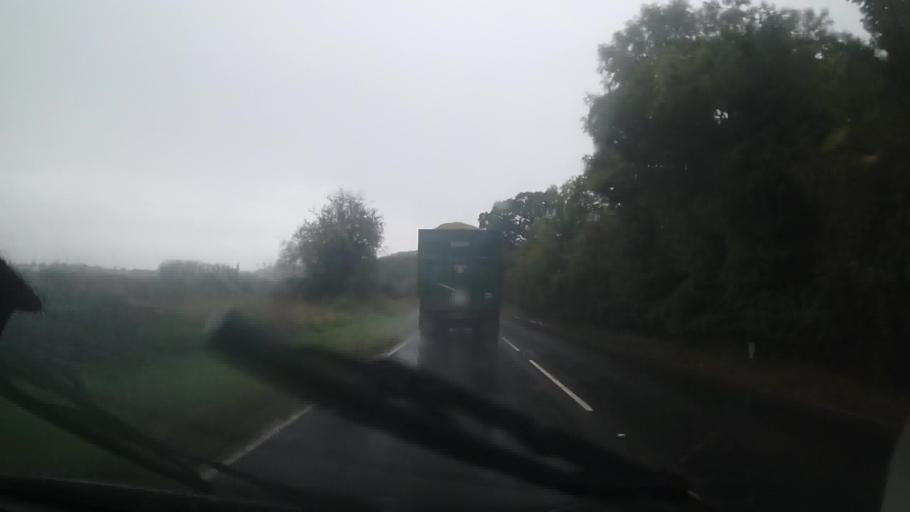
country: GB
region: England
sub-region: Worcestershire
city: Evesham
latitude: 52.1245
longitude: -1.9839
